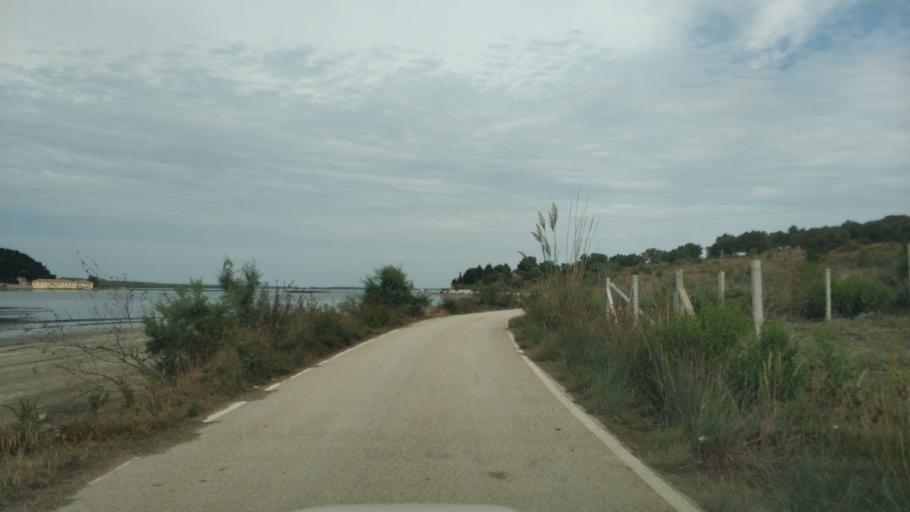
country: AL
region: Vlore
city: Vlore
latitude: 40.5133
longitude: 19.4078
